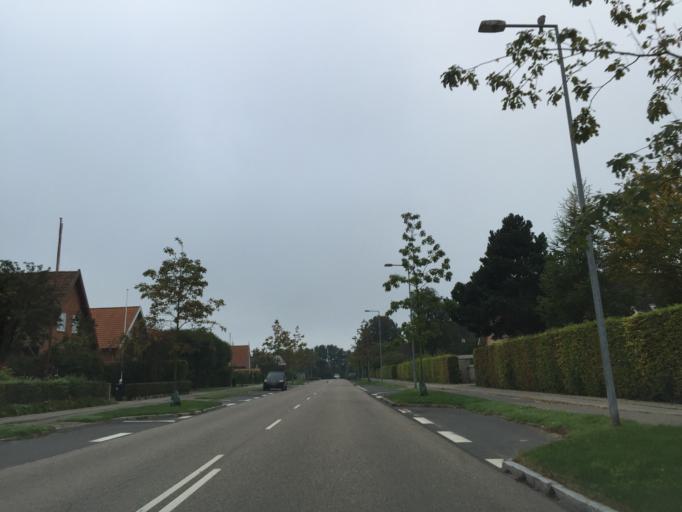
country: DK
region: South Denmark
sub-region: Sonderborg Kommune
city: Sonderborg
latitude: 54.9044
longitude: 9.8016
